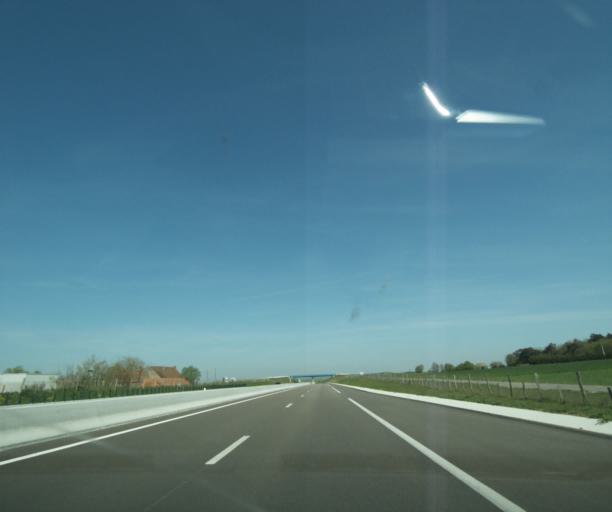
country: FR
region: Bourgogne
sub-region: Departement de la Nievre
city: Saint-Pierre-le-Moutier
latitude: 46.8145
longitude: 3.1234
